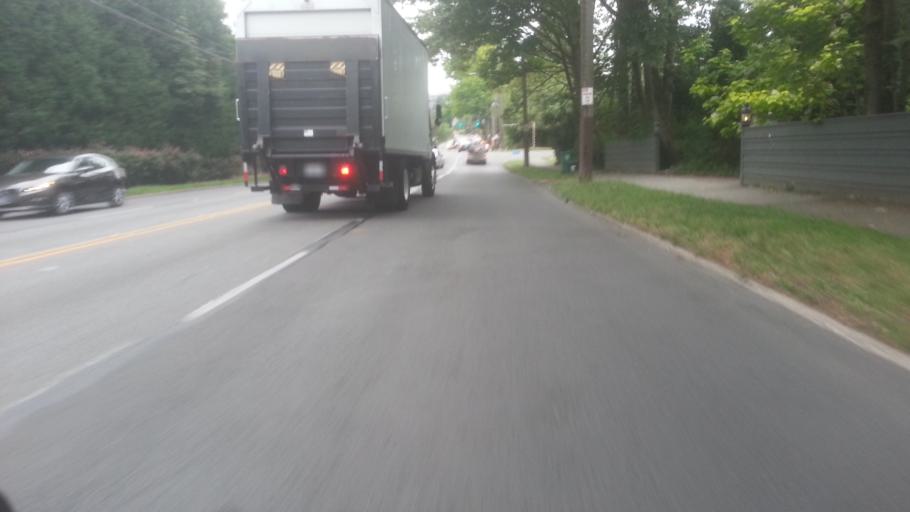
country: US
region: Washington
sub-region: King County
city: Seattle
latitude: 47.6339
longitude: -122.3015
